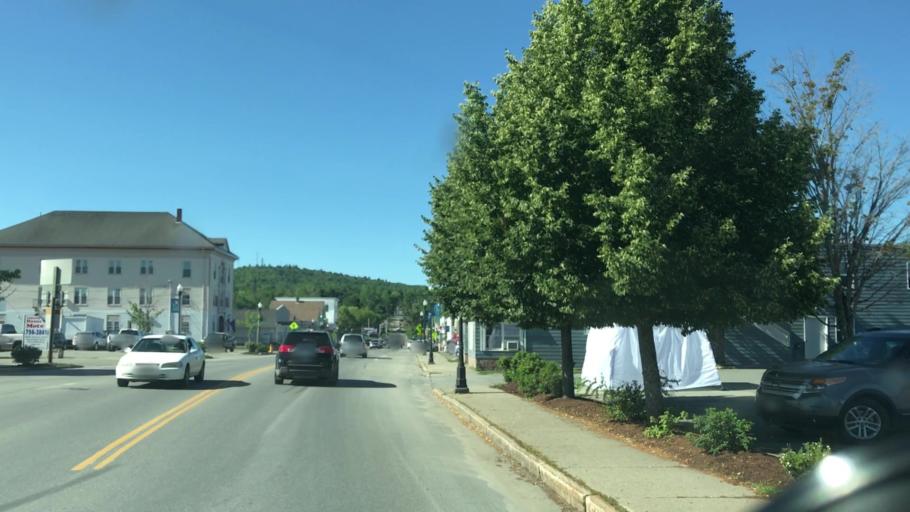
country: US
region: Maine
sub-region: Penobscot County
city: Lincoln
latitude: 45.3653
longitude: -68.5033
